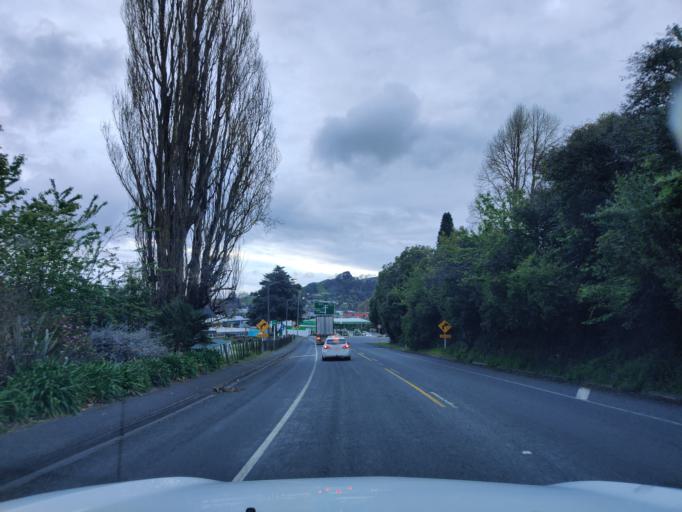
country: NZ
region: Waikato
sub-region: Otorohanga District
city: Otorohanga
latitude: -38.3399
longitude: 175.1674
